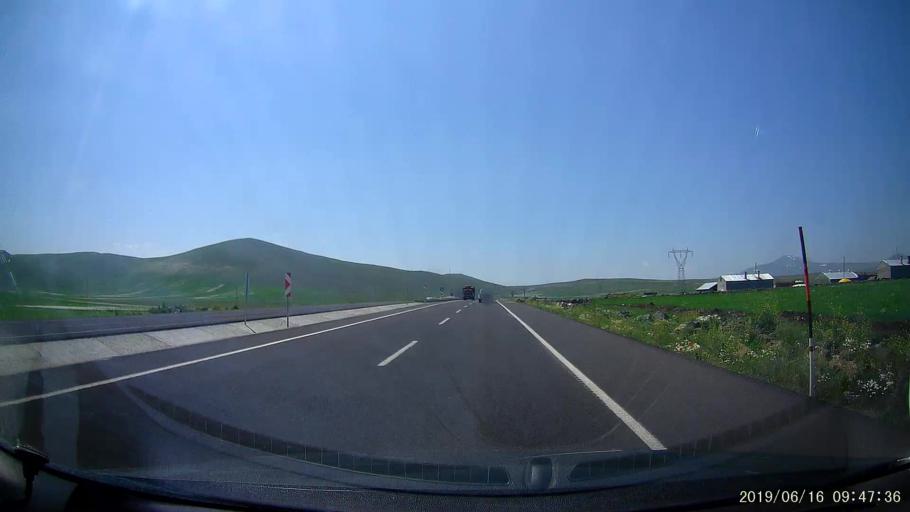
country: TR
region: Kars
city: Digor
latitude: 40.4443
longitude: 43.3458
